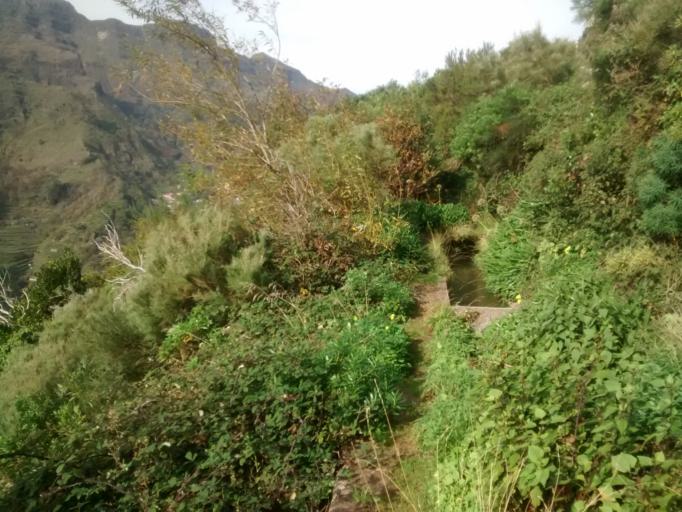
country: PT
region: Madeira
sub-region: Camara de Lobos
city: Curral das Freiras
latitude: 32.7211
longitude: -17.0247
